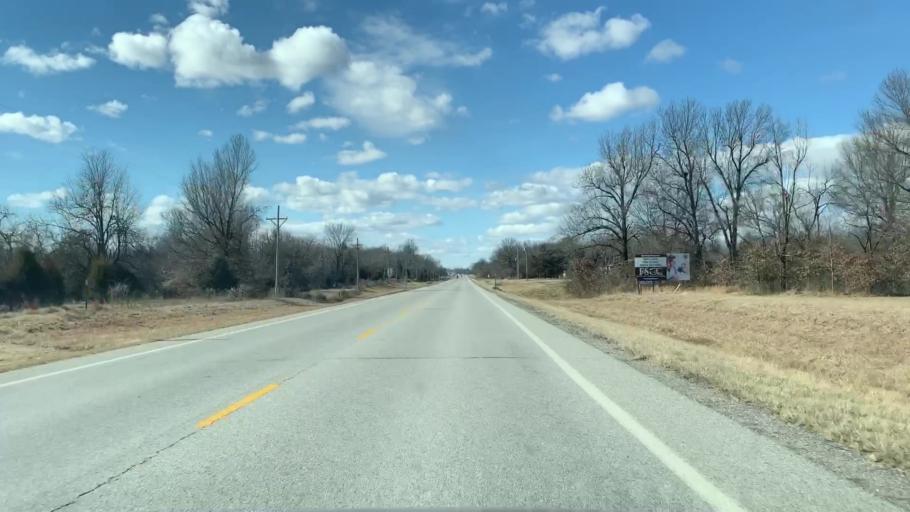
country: US
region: Kansas
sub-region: Cherokee County
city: Columbus
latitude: 37.1781
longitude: -94.8154
